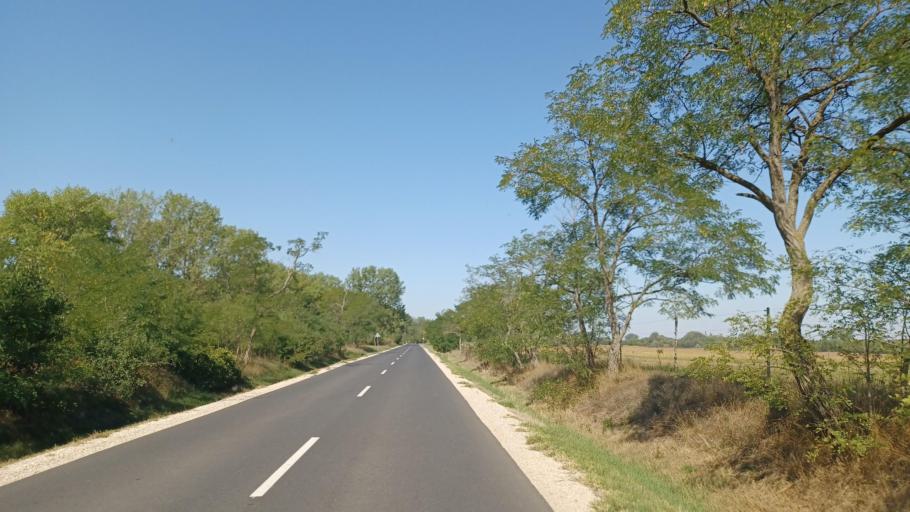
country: HU
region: Fejer
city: Alap
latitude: 46.7400
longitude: 18.7035
